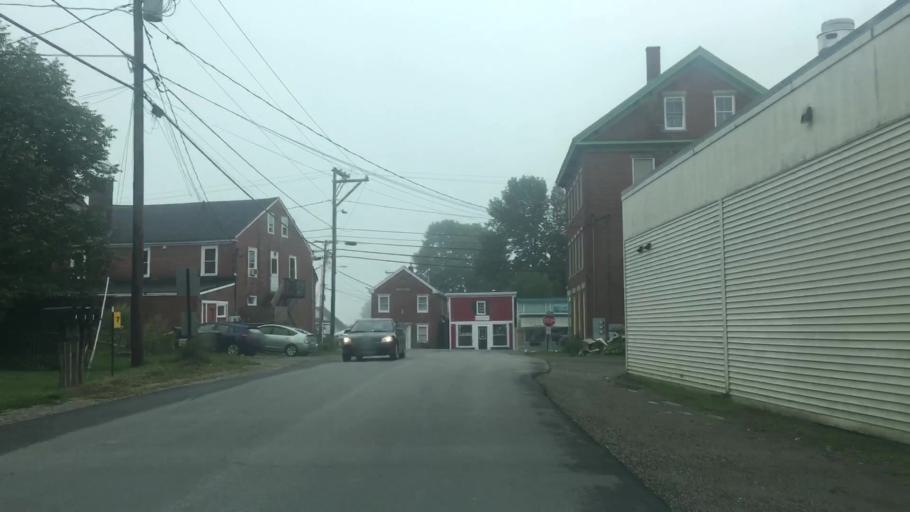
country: US
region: Maine
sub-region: Waldo County
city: Stockton Springs
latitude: 44.4589
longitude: -68.9262
